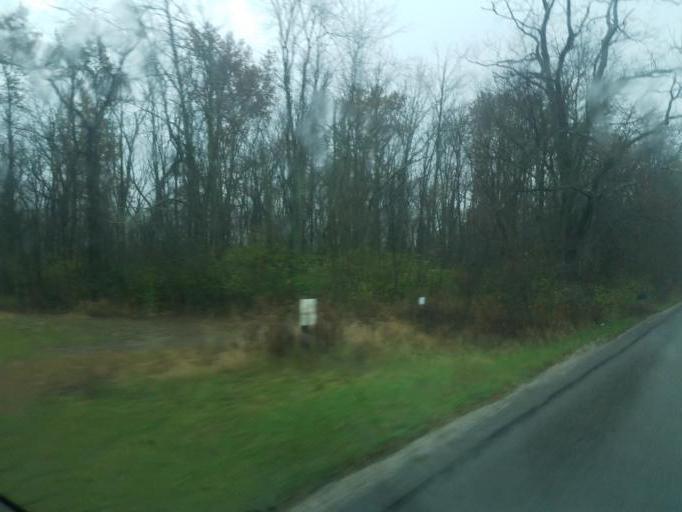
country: US
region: Ohio
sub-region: Delaware County
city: Ashley
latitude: 40.4134
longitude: -82.9000
